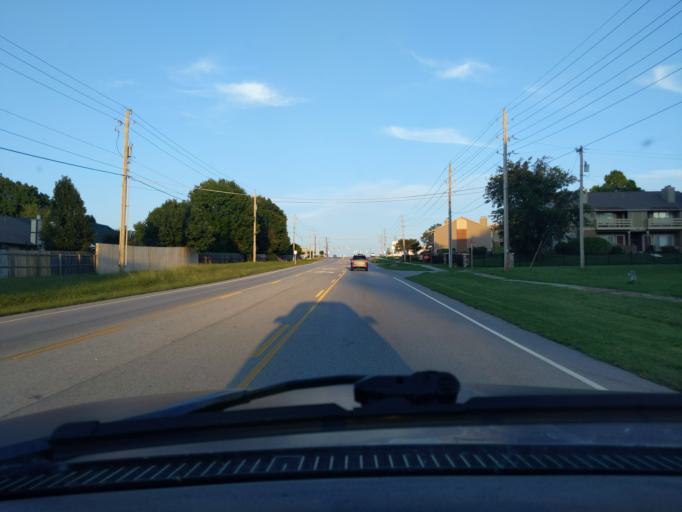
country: US
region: Oklahoma
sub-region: Tulsa County
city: Jenks
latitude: 36.0463
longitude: -95.9081
